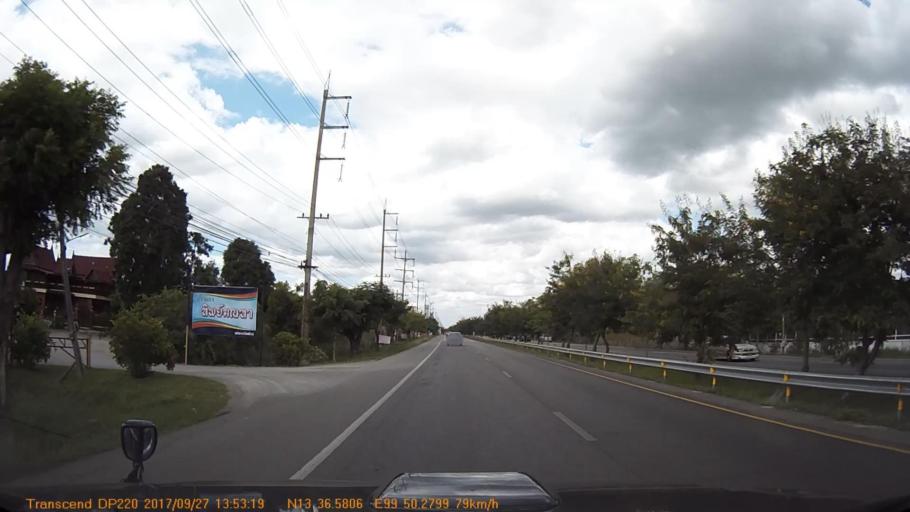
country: TH
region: Ratchaburi
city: Ratchaburi
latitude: 13.6099
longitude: 99.8381
